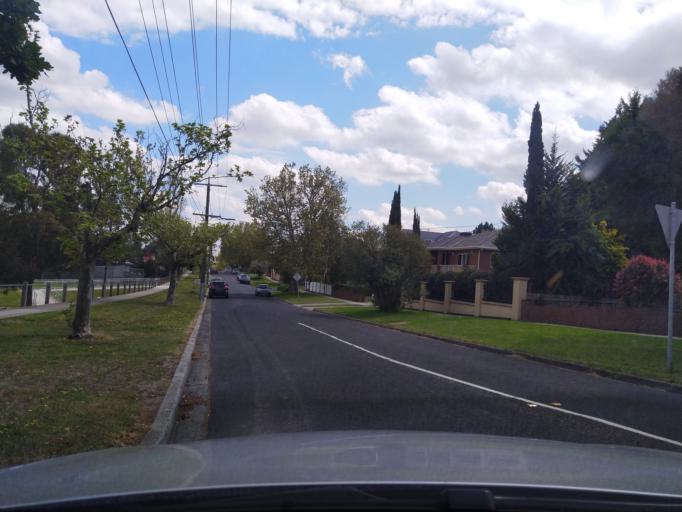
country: AU
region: Victoria
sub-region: Banyule
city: Heidelberg Heights
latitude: -37.7495
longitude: 145.0530
